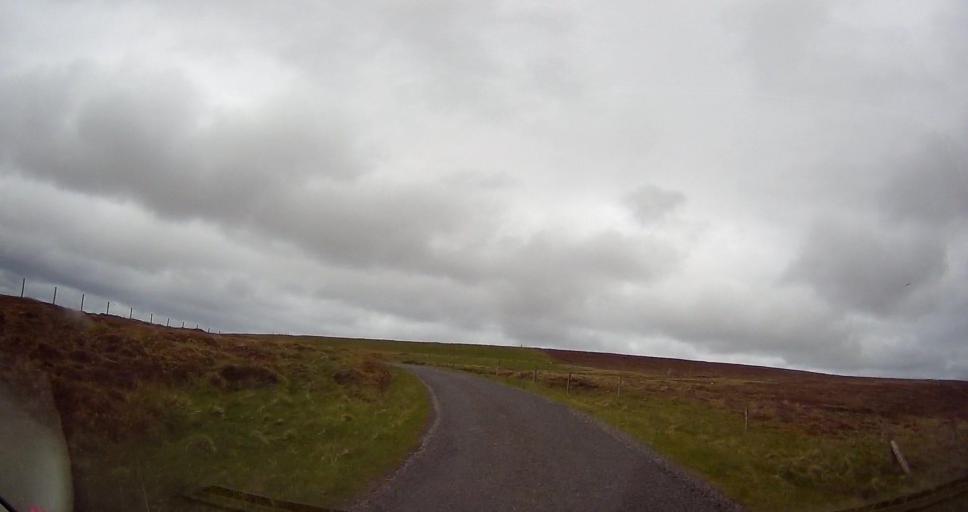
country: GB
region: Scotland
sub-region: Shetland Islands
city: Shetland
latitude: 60.7980
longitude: -0.8605
